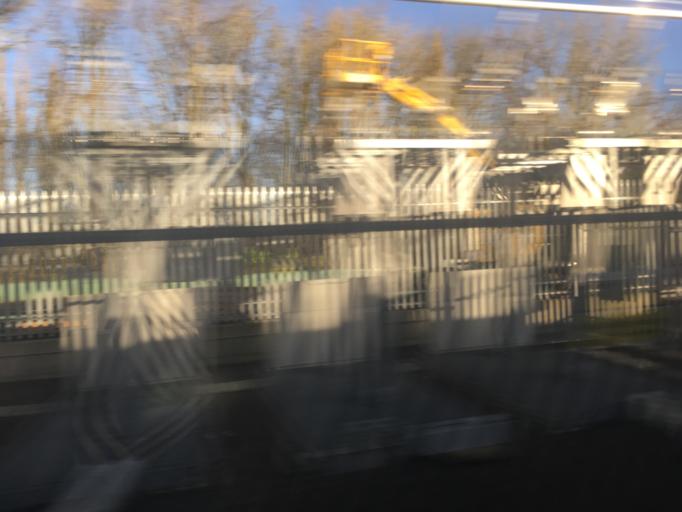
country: GB
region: England
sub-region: Wiltshire
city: Charlton
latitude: 51.5563
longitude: -2.0479
